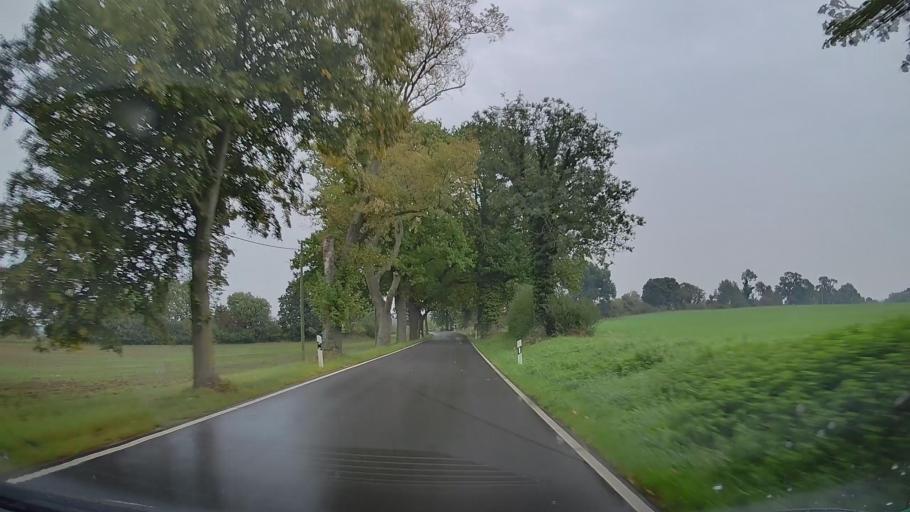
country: DE
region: Mecklenburg-Vorpommern
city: Kalkhorst
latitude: 53.9992
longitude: 11.0584
